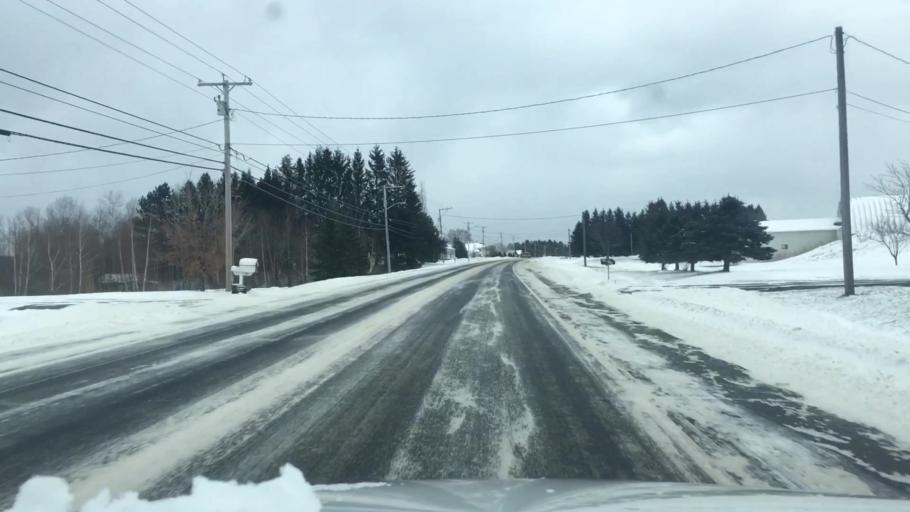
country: US
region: Maine
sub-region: Aroostook County
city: Madawaska
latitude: 47.3446
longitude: -68.2469
